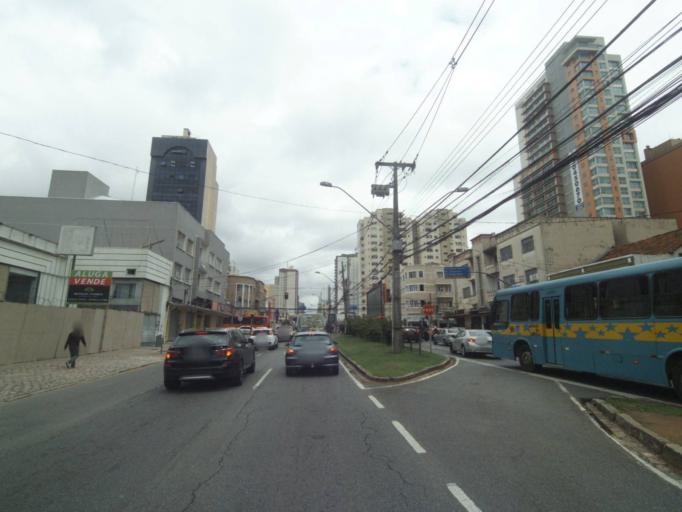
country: BR
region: Parana
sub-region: Curitiba
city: Curitiba
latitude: -25.4367
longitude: -49.2685
